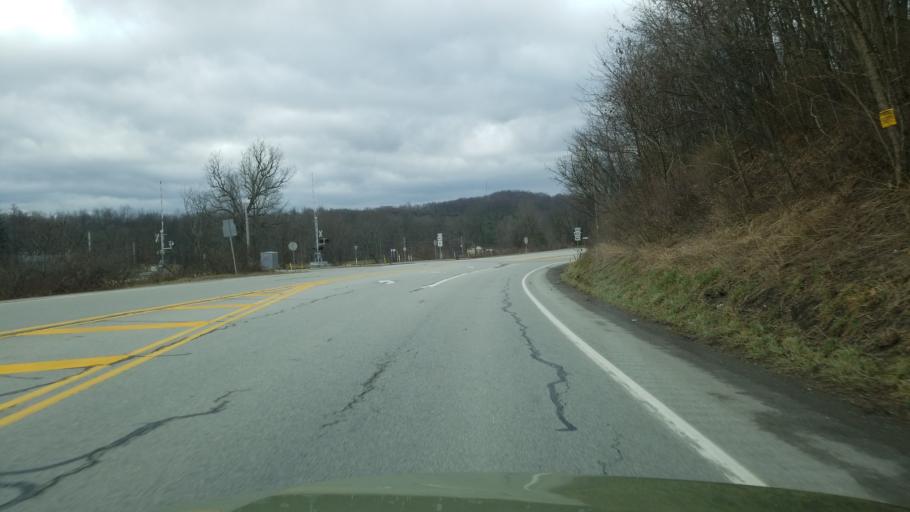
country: US
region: Pennsylvania
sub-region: Indiana County
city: Clymer
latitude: 40.7688
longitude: -79.0570
